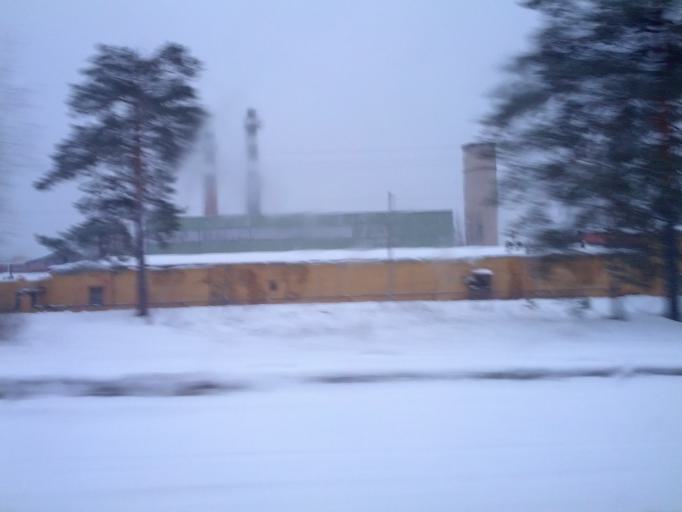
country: RU
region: Mariy-El
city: Surok
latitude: 56.3905
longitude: 48.1862
